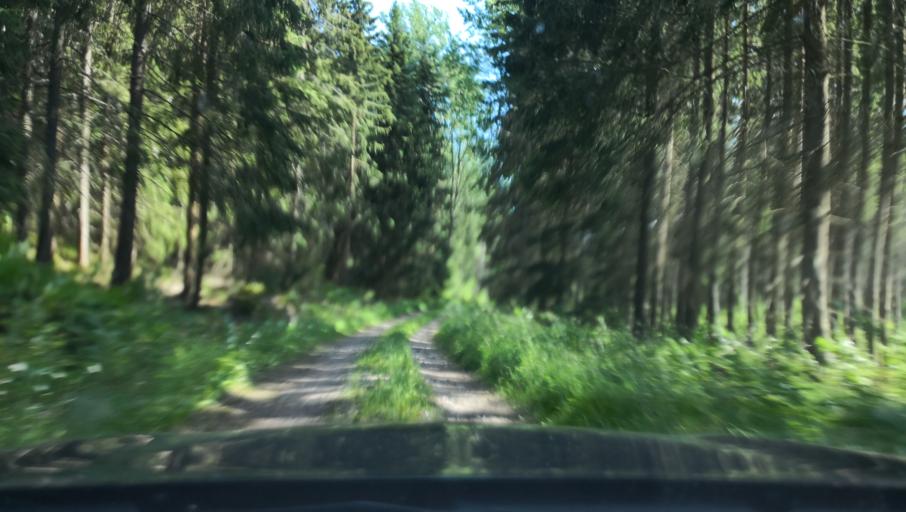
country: SE
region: Vaestmanland
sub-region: Kungsors Kommun
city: Kungsoer
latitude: 59.3410
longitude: 16.0612
